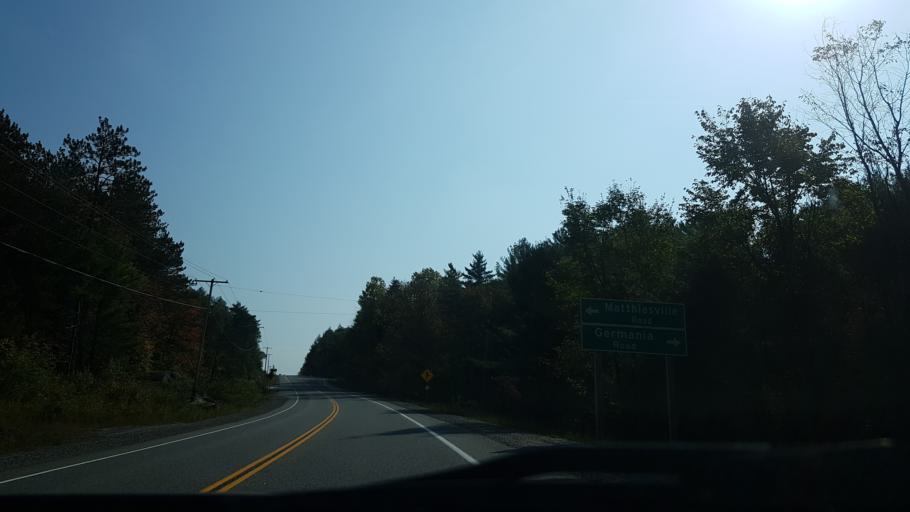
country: CA
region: Ontario
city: Bracebridge
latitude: 44.9836
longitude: -79.2657
